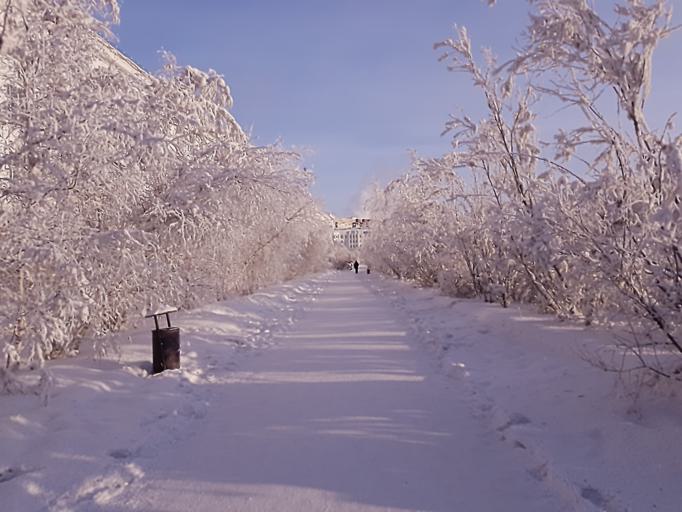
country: RU
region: Sakha
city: Yakutsk
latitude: 62.0189
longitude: 129.7081
